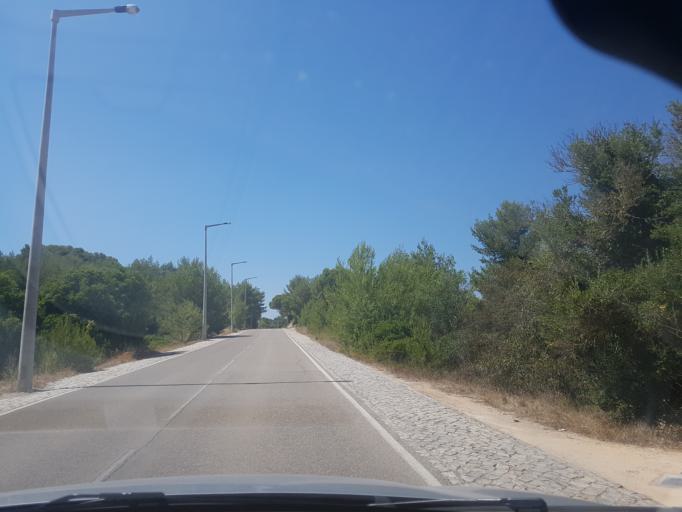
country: PT
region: Faro
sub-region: Lagoa
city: Carvoeiro
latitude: 37.0888
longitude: -8.4391
